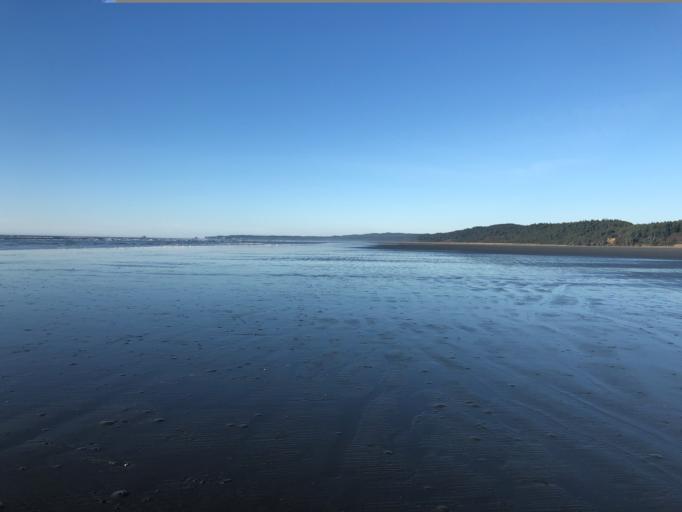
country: US
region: Washington
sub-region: Grays Harbor County
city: Ocean Shores
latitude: 47.2376
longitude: -124.2208
